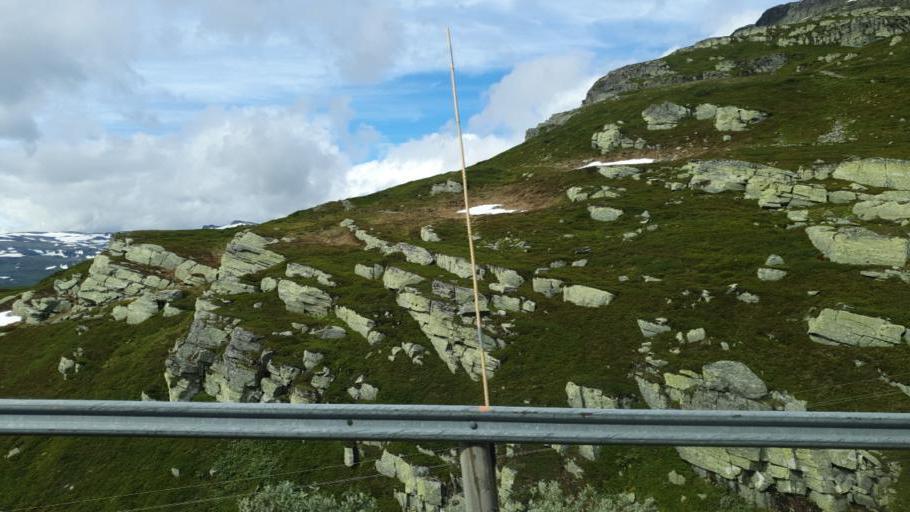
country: NO
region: Oppland
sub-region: Vestre Slidre
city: Slidre
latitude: 61.2883
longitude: 8.8135
